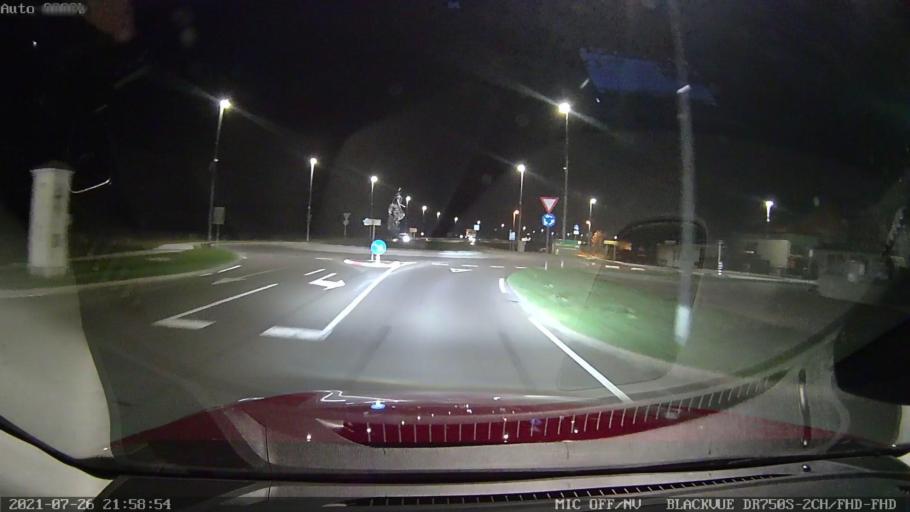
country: SI
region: Markovci
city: Markovci
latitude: 46.3983
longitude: 15.9317
